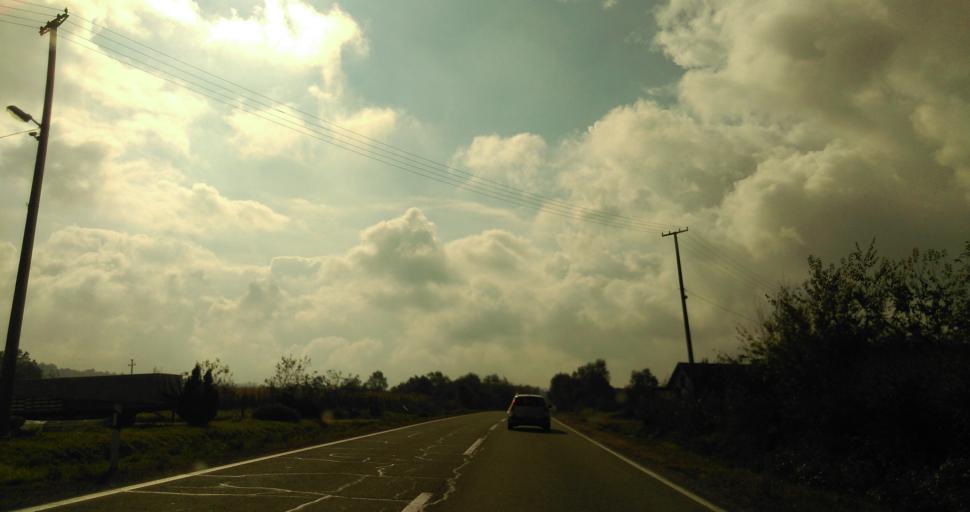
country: RS
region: Central Serbia
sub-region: Kolubarski Okrug
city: Ljig
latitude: 44.2766
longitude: 20.2811
